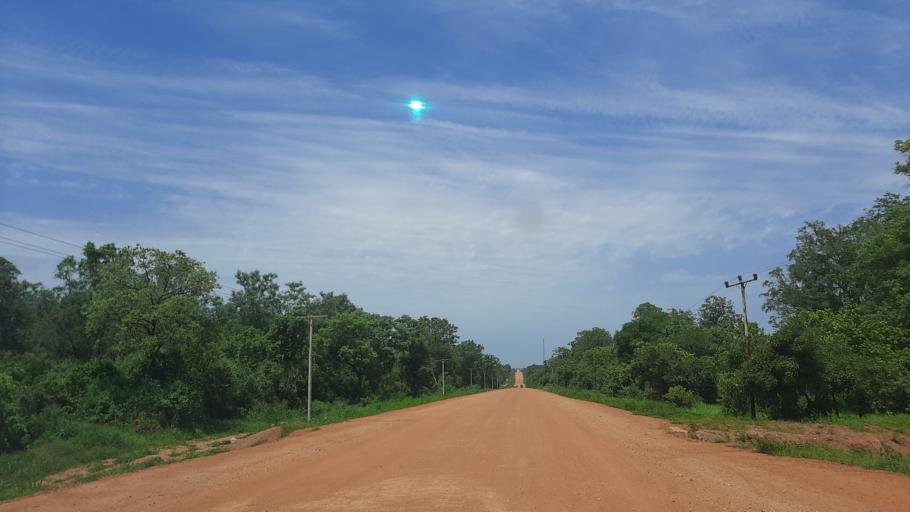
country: ET
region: Gambela
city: Gambela
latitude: 8.0752
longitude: 34.5895
